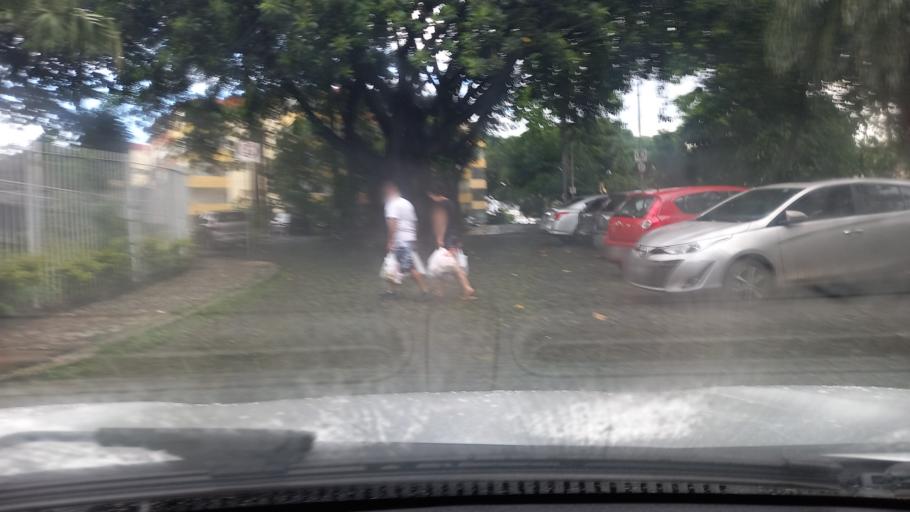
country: BR
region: Minas Gerais
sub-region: Belo Horizonte
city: Belo Horizonte
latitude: -19.9033
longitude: -43.9459
